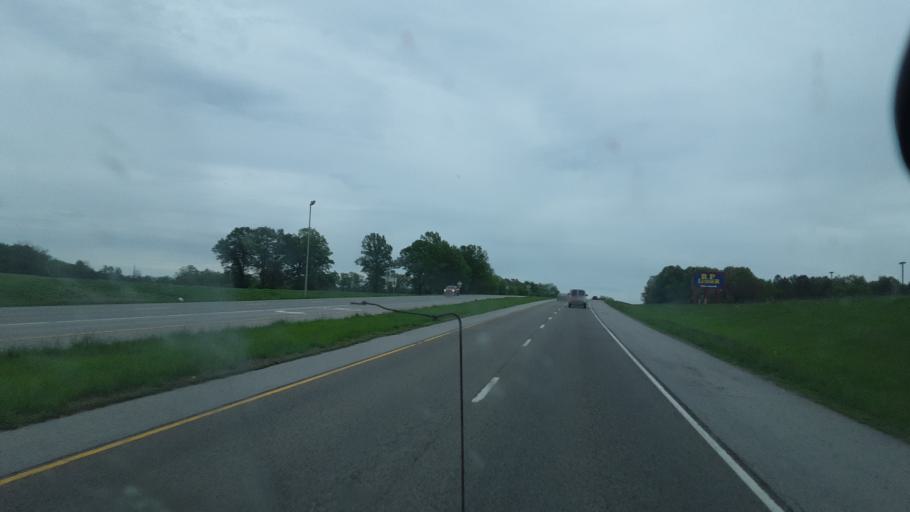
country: US
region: Illinois
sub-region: Jackson County
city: Carbondale
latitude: 37.7574
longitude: -89.2722
